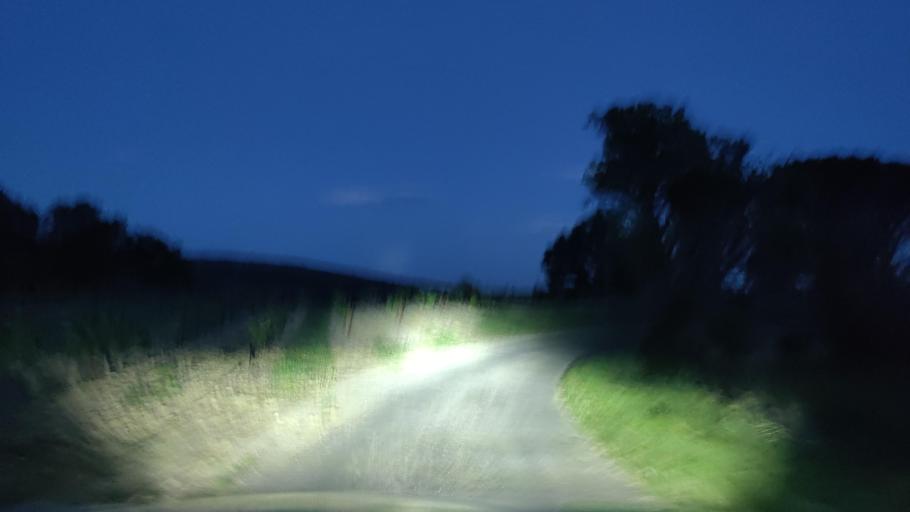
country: FR
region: Languedoc-Roussillon
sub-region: Departement des Pyrenees-Orientales
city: Estagel
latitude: 42.8747
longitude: 2.7302
